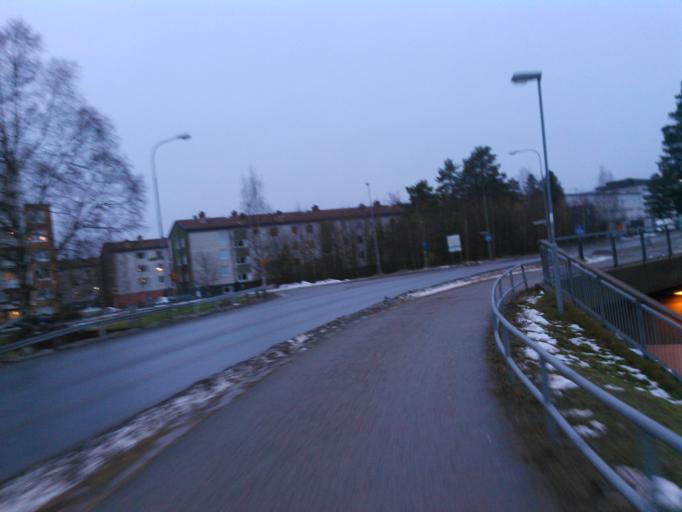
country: SE
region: Vaesterbotten
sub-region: Umea Kommun
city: Umea
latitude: 63.8137
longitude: 20.3037
